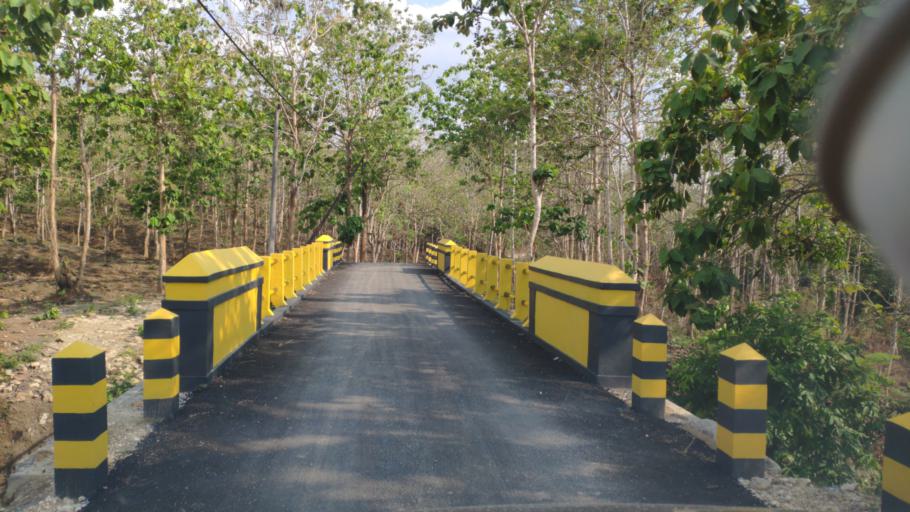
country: ID
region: Central Java
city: Semanggi
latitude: -7.0646
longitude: 111.4319
